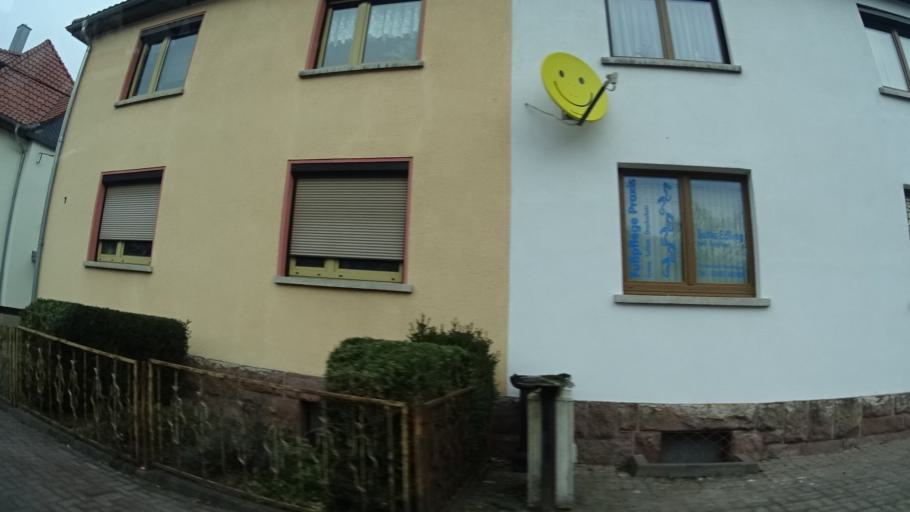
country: DE
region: Thuringia
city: Zella-Mehlis
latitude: 50.6596
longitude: 10.6543
